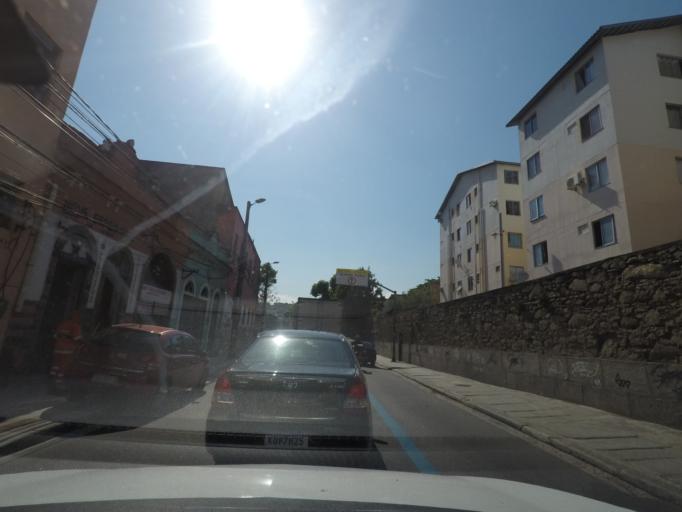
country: BR
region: Rio de Janeiro
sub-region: Rio De Janeiro
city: Rio de Janeiro
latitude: -22.9141
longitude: -43.2000
